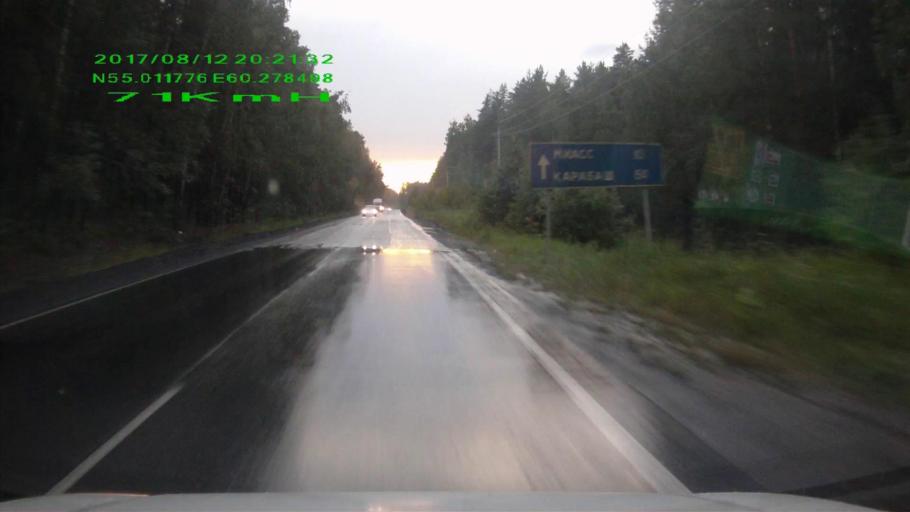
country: RU
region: Chelyabinsk
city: Chebarkul'
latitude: 55.0118
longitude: 60.2785
